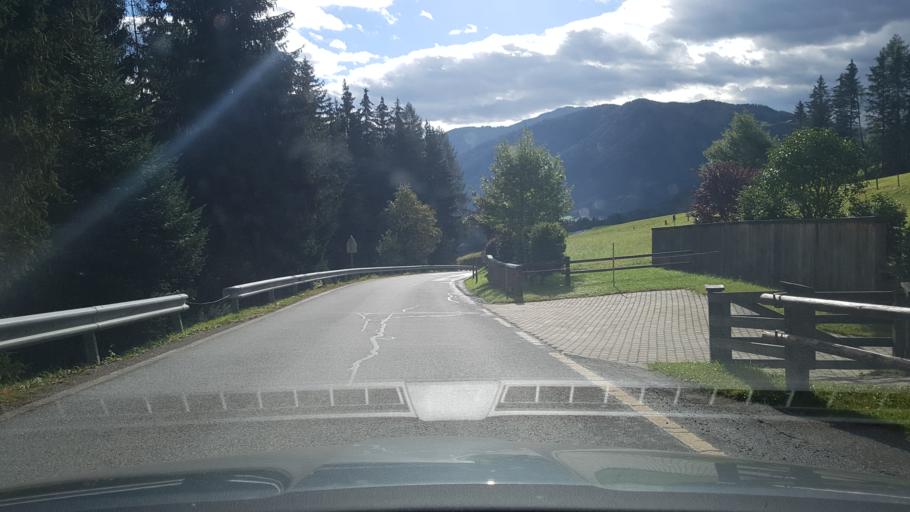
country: AT
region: Styria
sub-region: Politischer Bezirk Murau
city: Schoder
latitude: 47.2052
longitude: 14.1083
